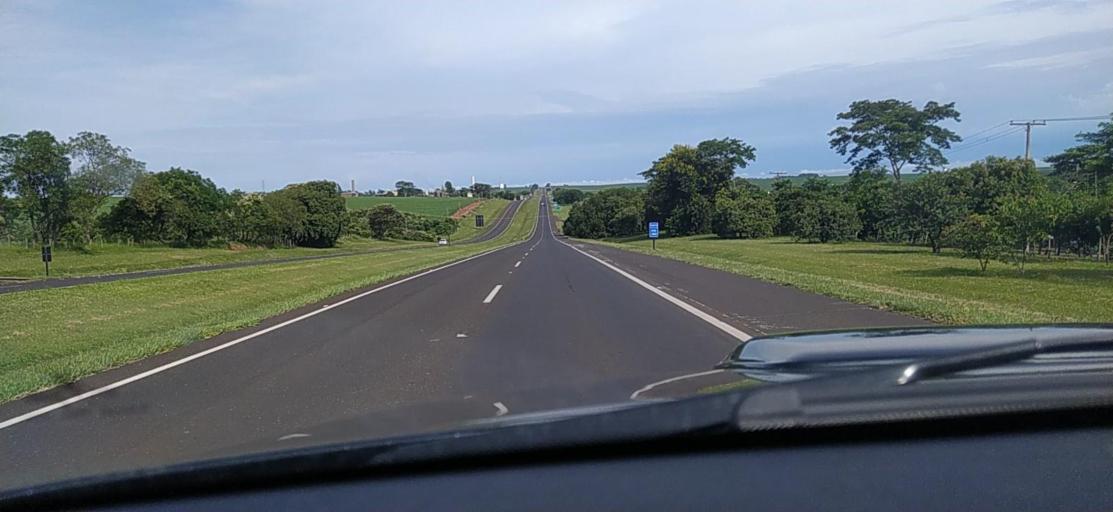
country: BR
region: Sao Paulo
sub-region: Catanduva
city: Catanduva
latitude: -21.1305
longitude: -49.0246
